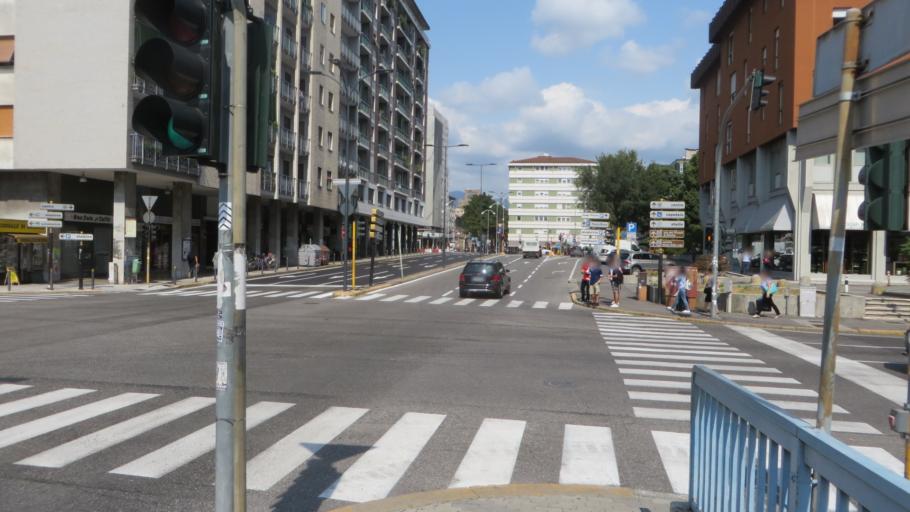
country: IT
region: Lombardy
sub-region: Provincia di Brescia
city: Brescia
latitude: 45.5325
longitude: 10.2177
